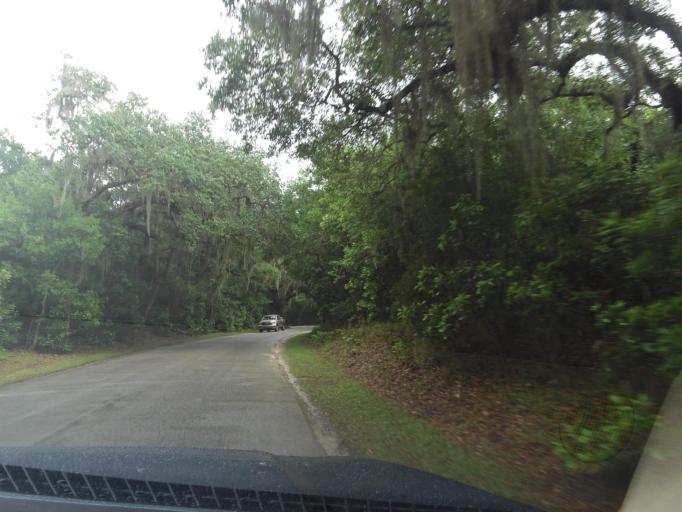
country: US
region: Florida
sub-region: Nassau County
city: Fernandina Beach
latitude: 30.7017
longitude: -81.4474
